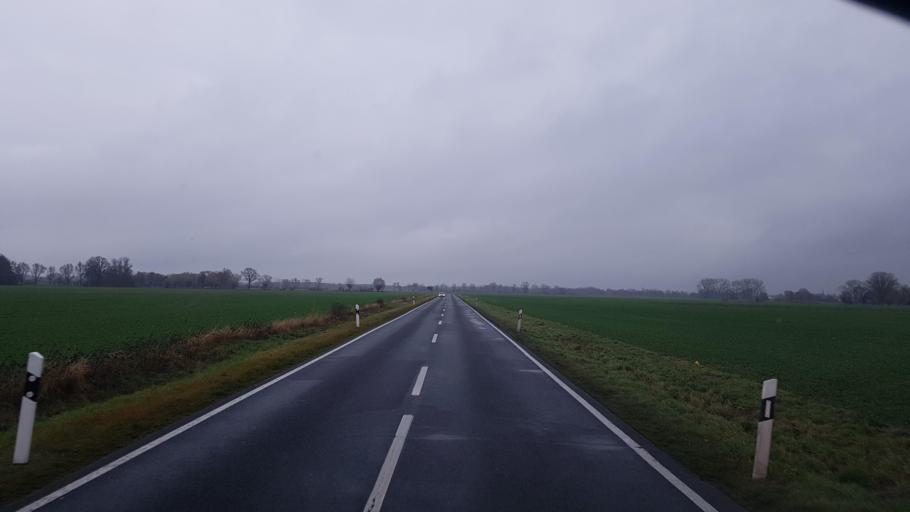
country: DE
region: Brandenburg
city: Roskow
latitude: 52.4647
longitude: 12.6832
